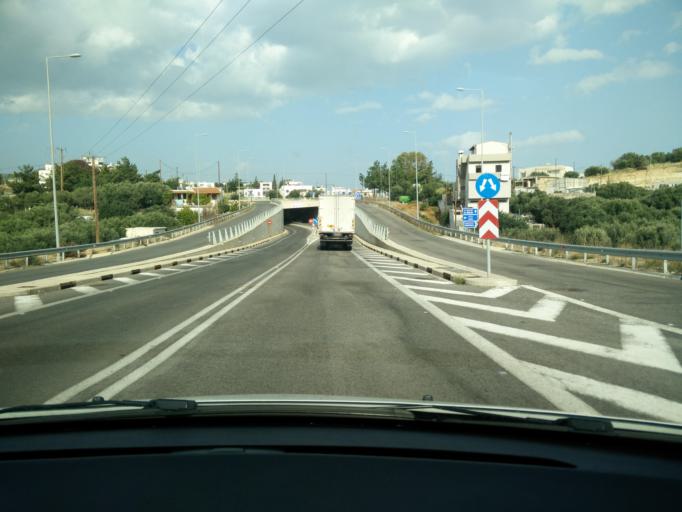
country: GR
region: Crete
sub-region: Nomos Lasithiou
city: Agios Nikolaos
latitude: 35.1831
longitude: 25.7041
